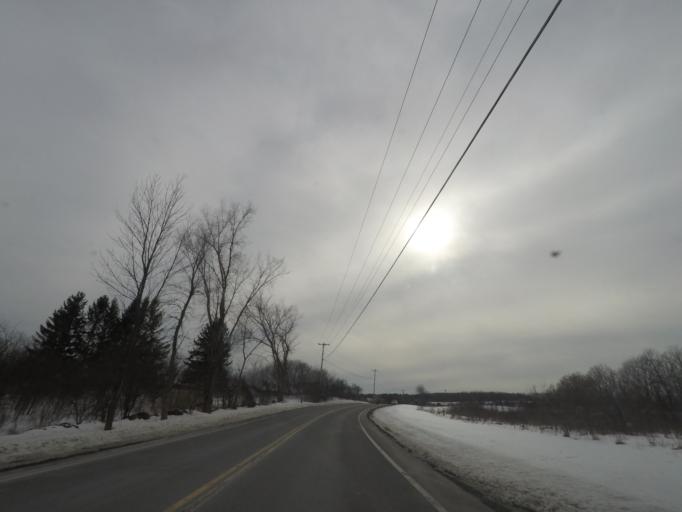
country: US
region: New York
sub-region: Albany County
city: Altamont
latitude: 42.6805
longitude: -74.0746
